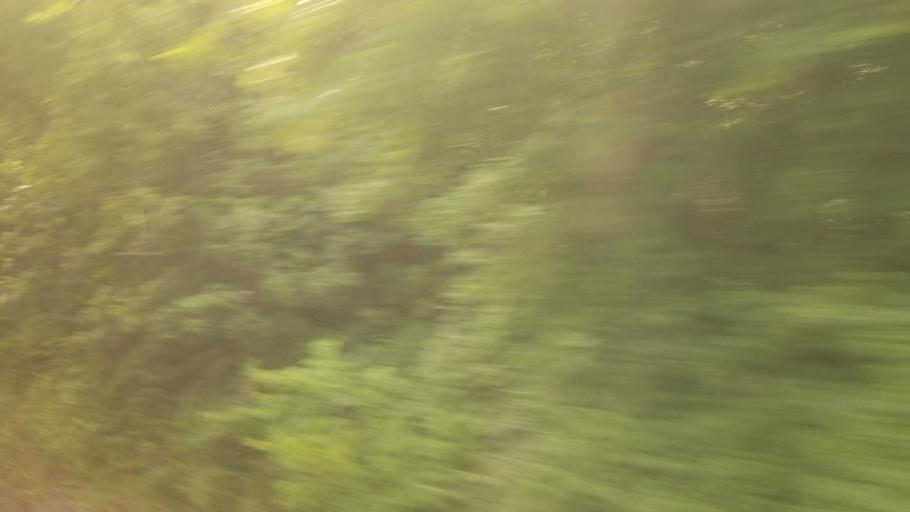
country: US
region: Missouri
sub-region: Jackson County
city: East Independence
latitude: 39.1565
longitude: -94.3785
